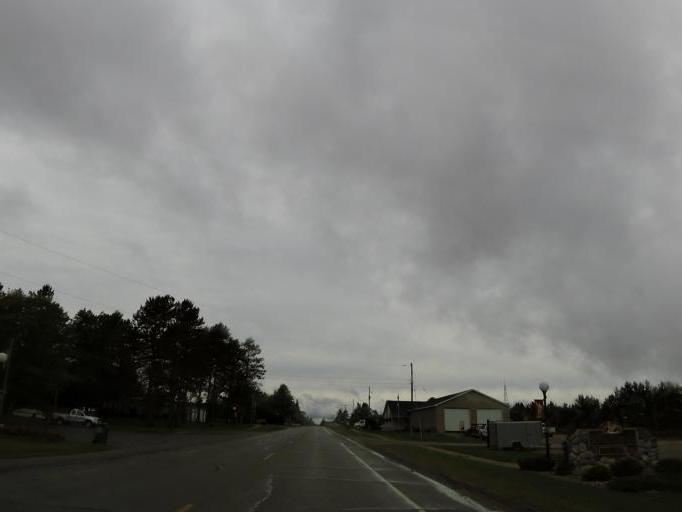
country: US
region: Michigan
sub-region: Roscommon County
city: Roscommon
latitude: 44.4920
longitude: -84.5813
